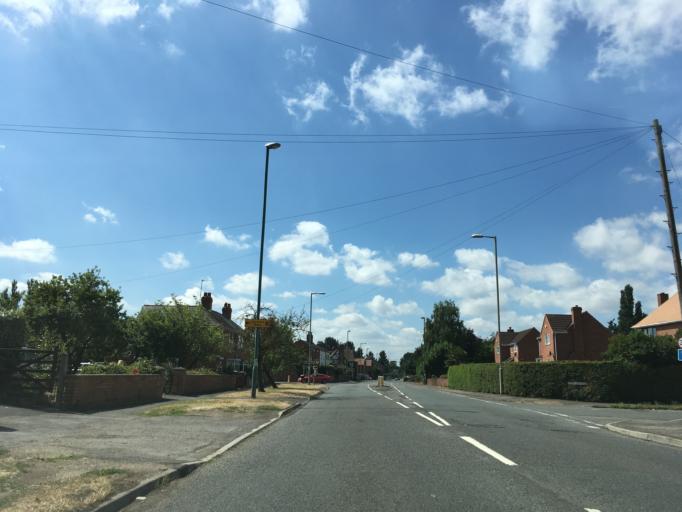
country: GB
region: England
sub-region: Gloucestershire
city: Gloucester
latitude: 51.8860
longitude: -2.2359
